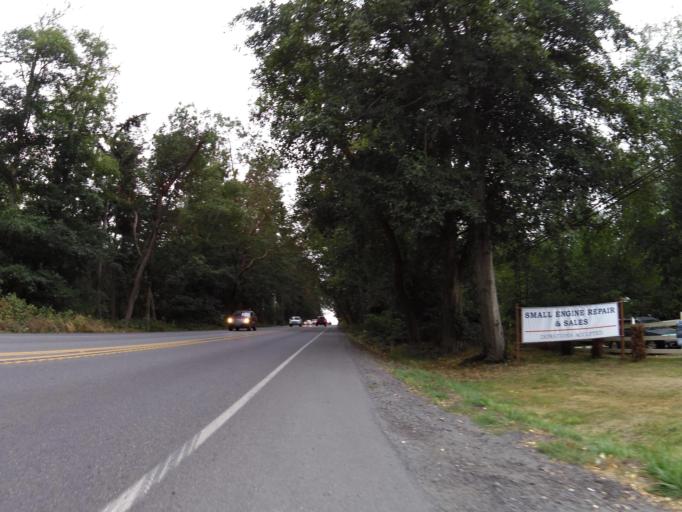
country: US
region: Washington
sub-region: Jefferson County
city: Port Hadlock-Irondale
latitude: 48.0870
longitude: -122.8167
